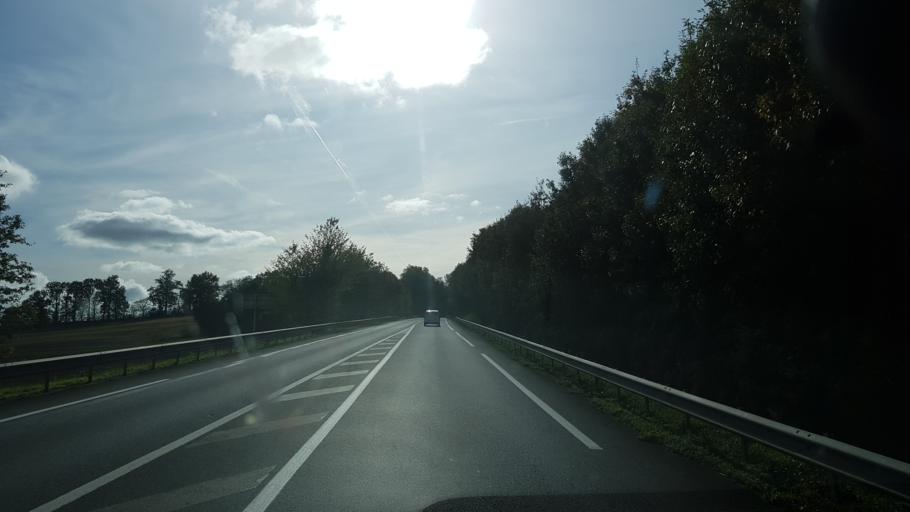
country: FR
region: Poitou-Charentes
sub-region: Departement de la Charente
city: Confolens
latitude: 45.9954
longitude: 0.6299
